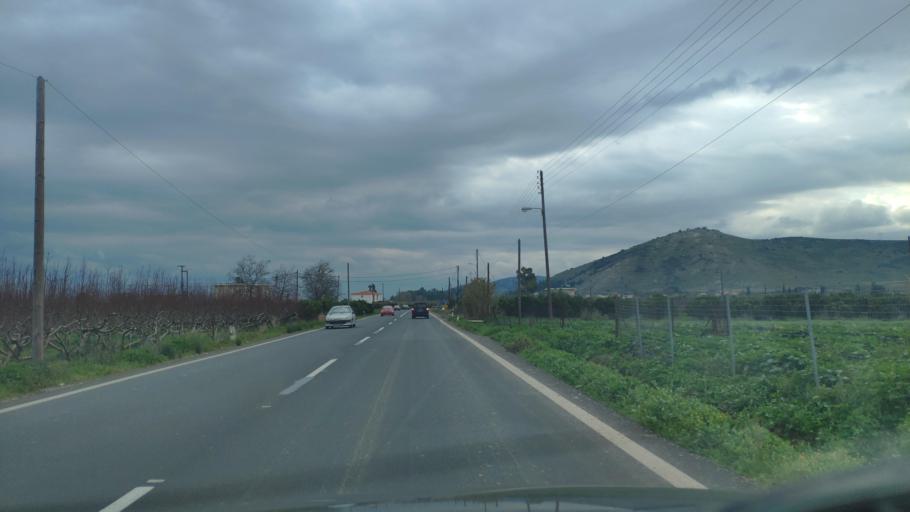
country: GR
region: Peloponnese
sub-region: Nomos Argolidos
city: Nea Kios
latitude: 37.5702
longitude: 22.7093
